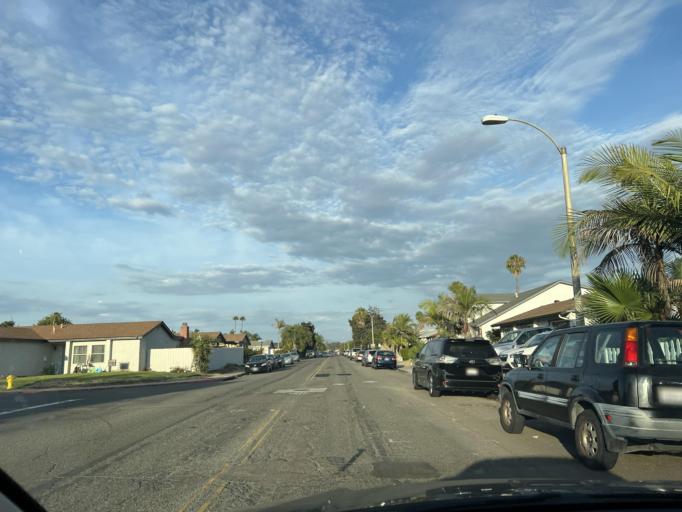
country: US
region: California
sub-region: San Diego County
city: Fairbanks Ranch
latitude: 32.9021
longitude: -117.1430
